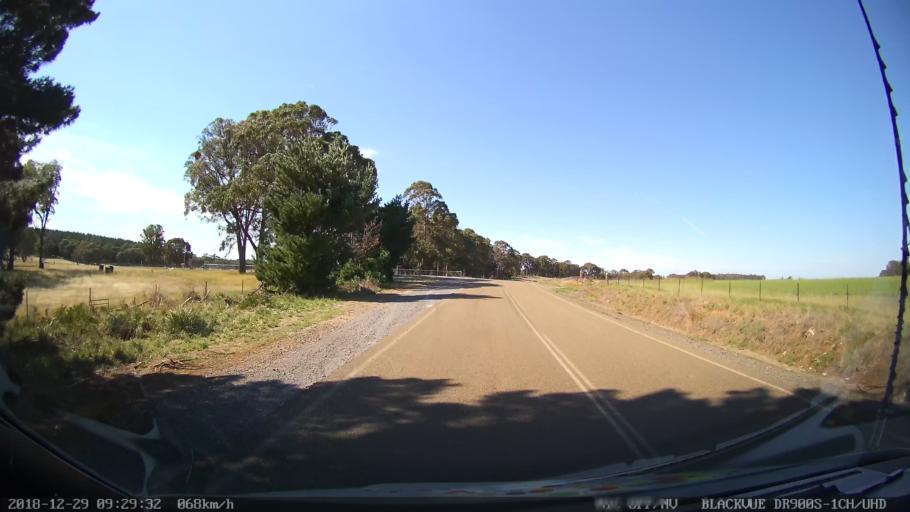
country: AU
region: New South Wales
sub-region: Upper Lachlan Shire
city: Crookwell
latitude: -34.5893
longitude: 149.3744
